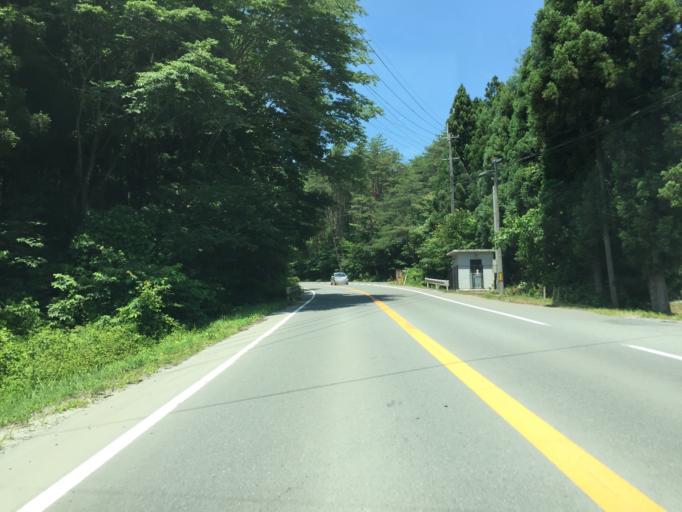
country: JP
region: Miyagi
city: Marumori
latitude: 37.7811
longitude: 140.8234
